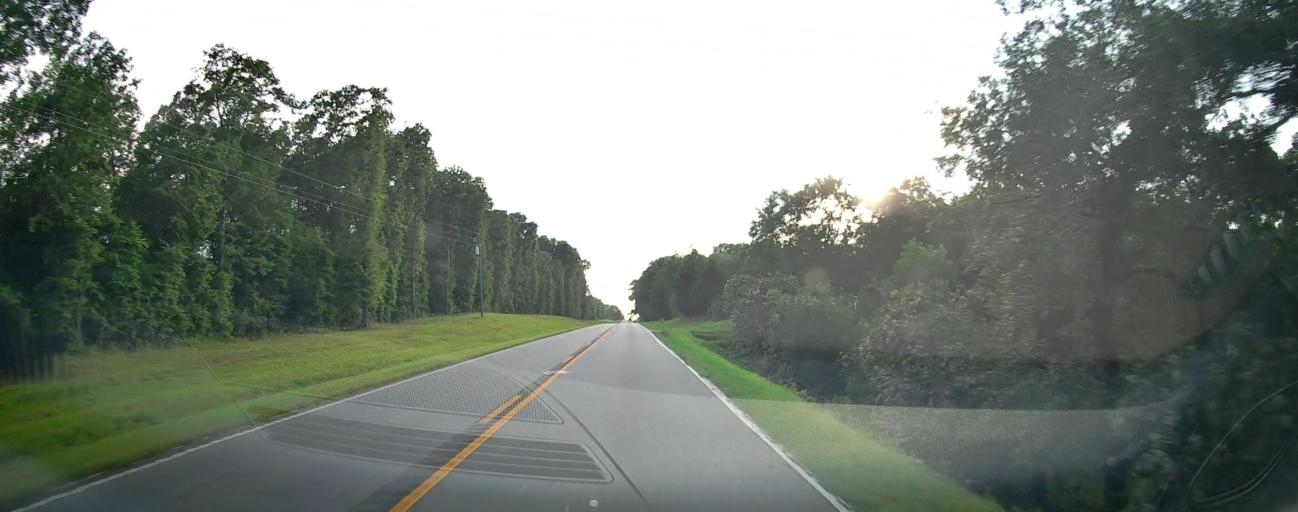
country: US
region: Georgia
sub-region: Peach County
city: Fort Valley
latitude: 32.5583
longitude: -83.9290
